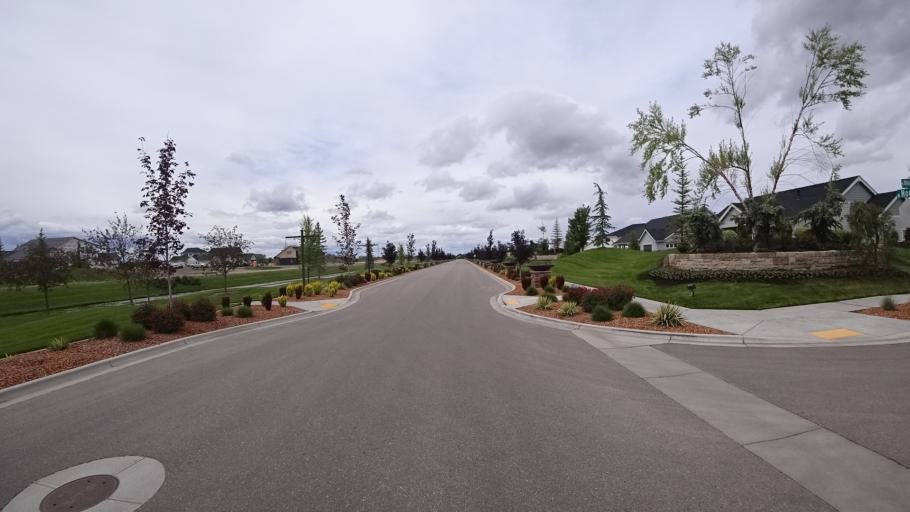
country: US
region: Idaho
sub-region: Ada County
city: Star
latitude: 43.7030
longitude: -116.4372
